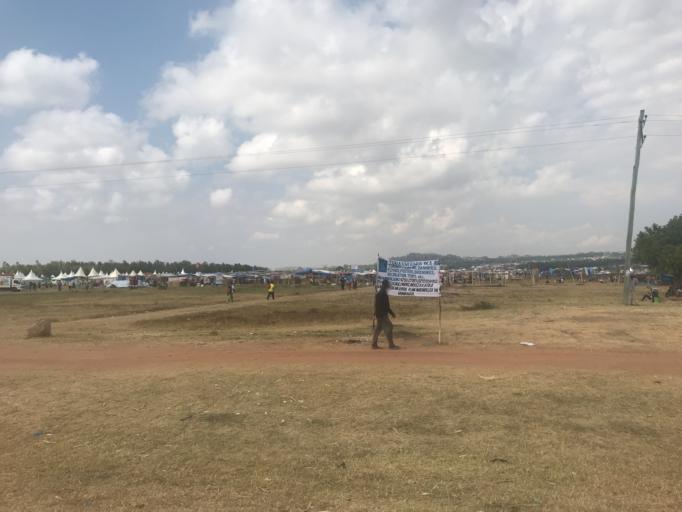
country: TZ
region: Mwanza
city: Mwanza
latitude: -2.5506
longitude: 33.0103
